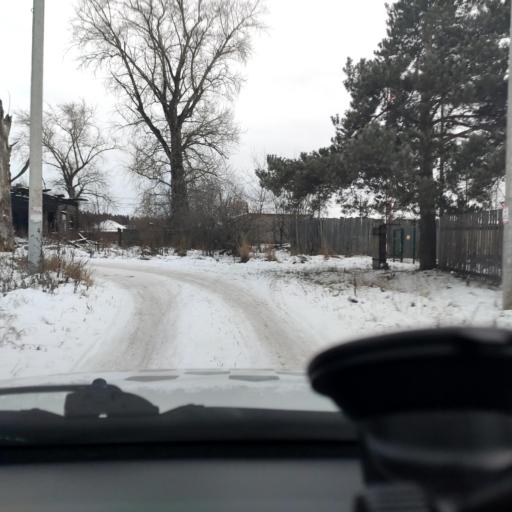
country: RU
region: Perm
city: Froly
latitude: 57.9544
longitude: 56.2868
